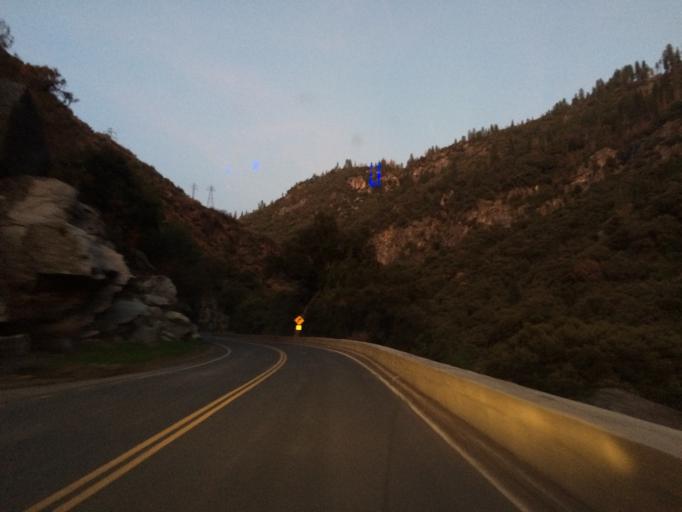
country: US
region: California
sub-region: Mariposa County
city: Yosemite Valley
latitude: 37.6759
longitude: -119.7421
